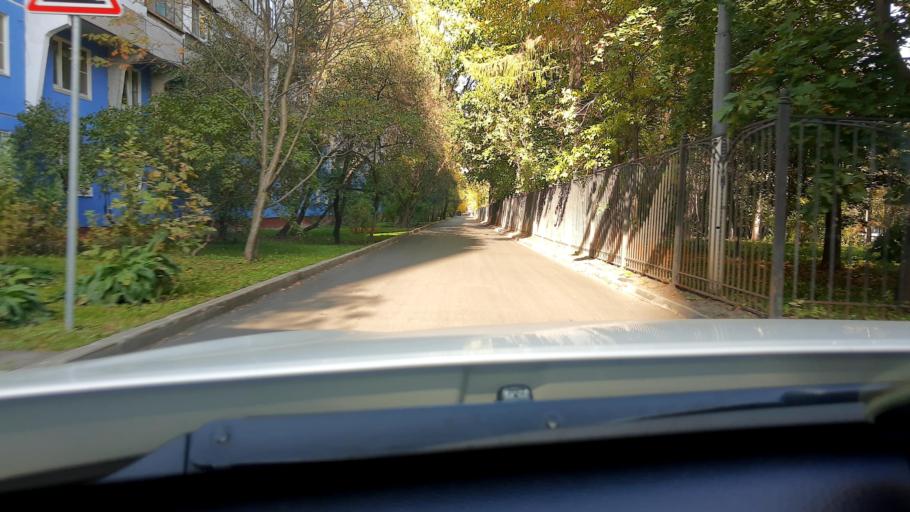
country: RU
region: Moskovskaya
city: Vostochnoe Degunino
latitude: 55.8888
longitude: 37.5632
